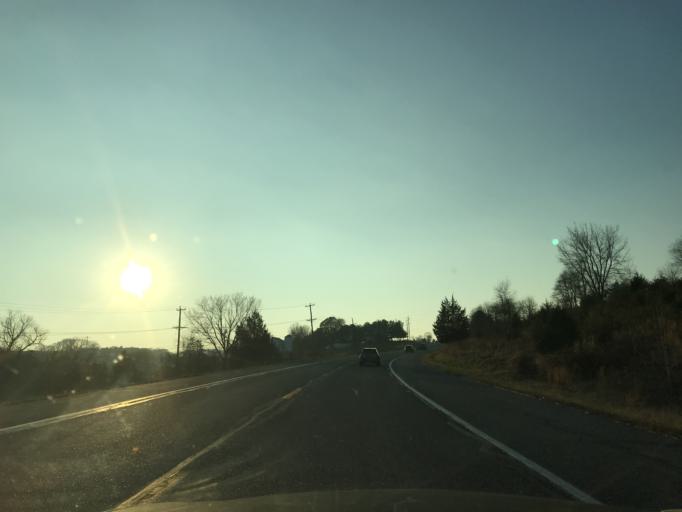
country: US
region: Pennsylvania
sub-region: York County
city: Susquehanna Trails
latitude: 39.6817
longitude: -76.3794
